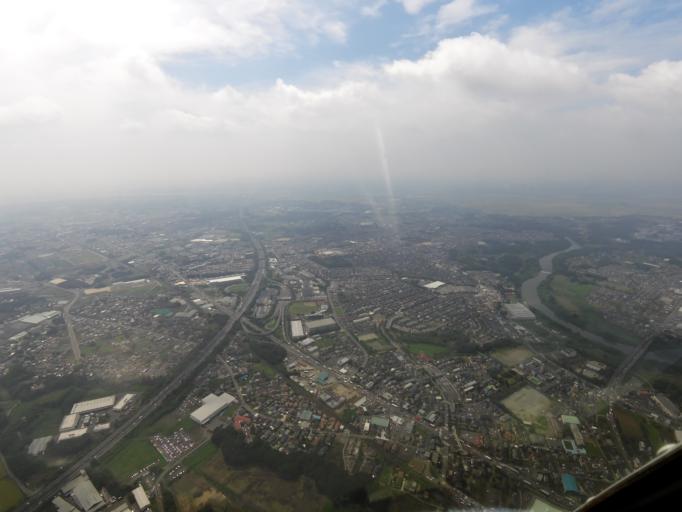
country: JP
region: Ibaraki
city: Mitsukaido
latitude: 35.9837
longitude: 139.9879
